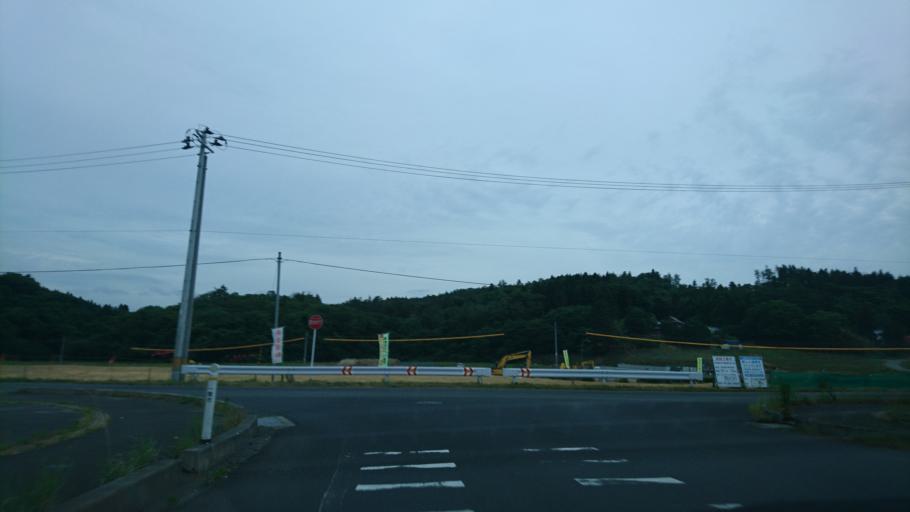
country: JP
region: Iwate
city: Ichinoseki
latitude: 38.9330
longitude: 141.1720
